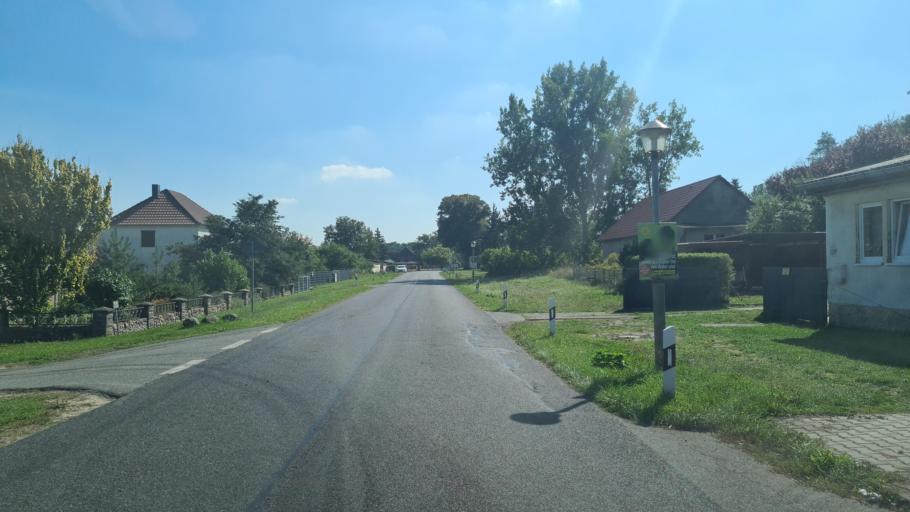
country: DE
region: Brandenburg
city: Friesack
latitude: 52.7141
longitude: 12.6418
